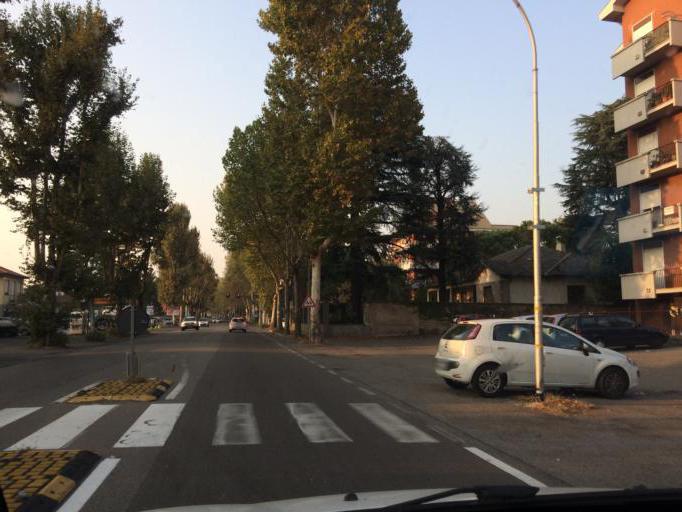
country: IT
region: Lombardy
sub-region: Provincia di Varese
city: Castellanza
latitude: 45.6092
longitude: 8.8893
